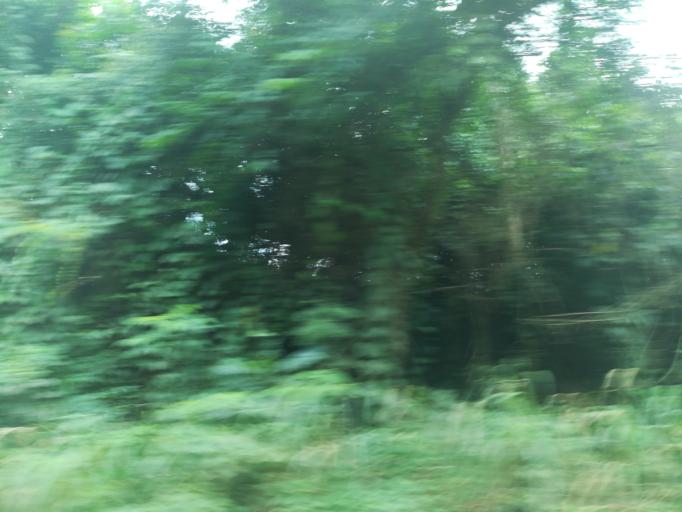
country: NG
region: Lagos
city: Ejirin
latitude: 6.6453
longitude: 3.7255
